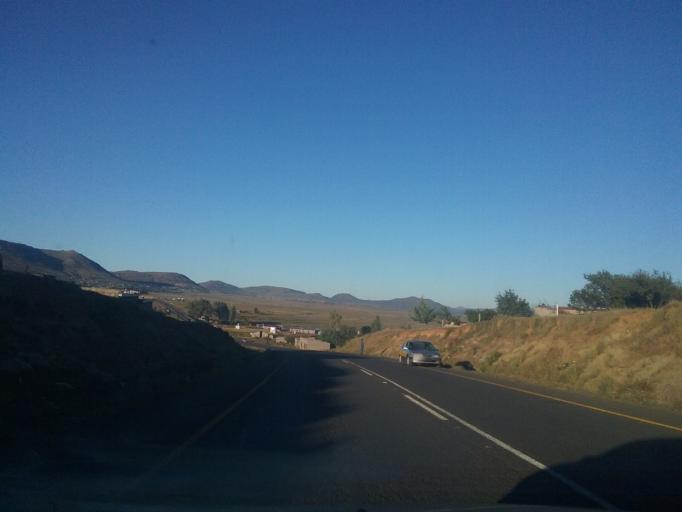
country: LS
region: Mohale's Hoek District
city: Mohale's Hoek
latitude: -30.1523
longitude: 27.4418
